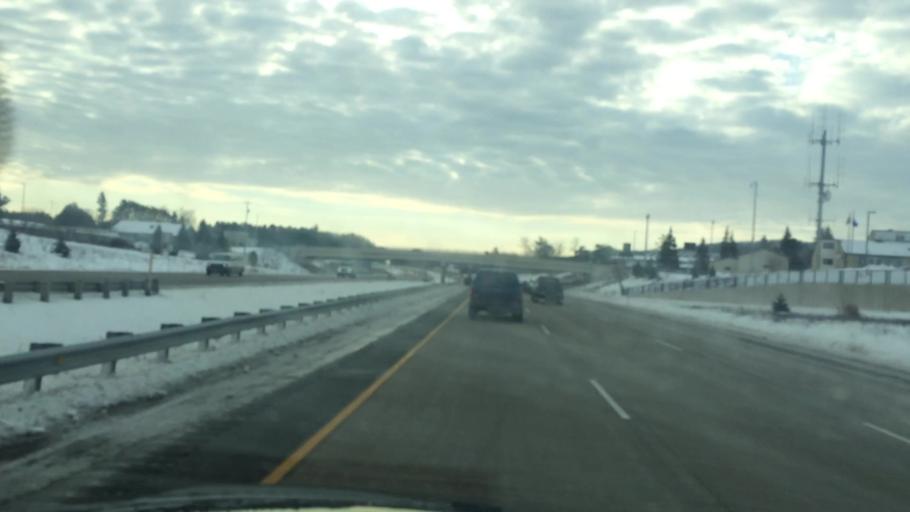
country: US
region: Wisconsin
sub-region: Marathon County
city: Rib Mountain
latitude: 44.9326
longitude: -89.6646
